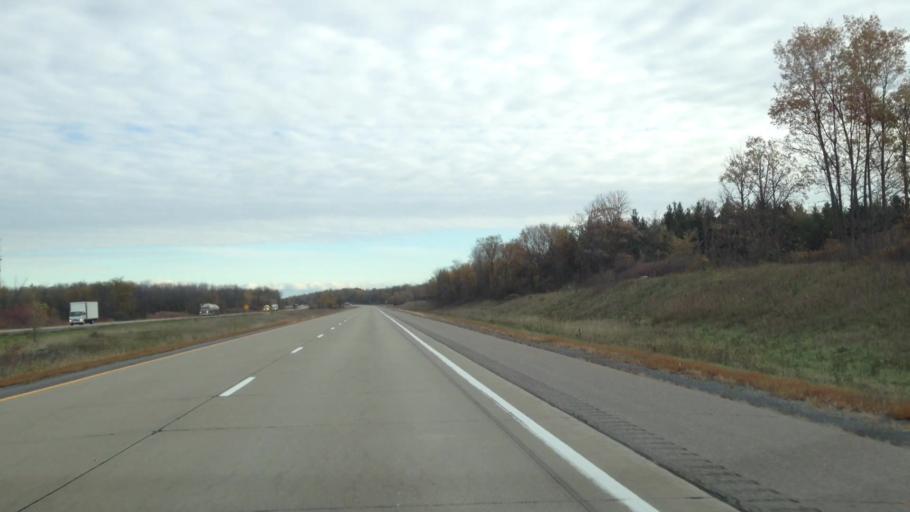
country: CA
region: Ontario
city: Hawkesbury
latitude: 45.3854
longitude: -74.7936
